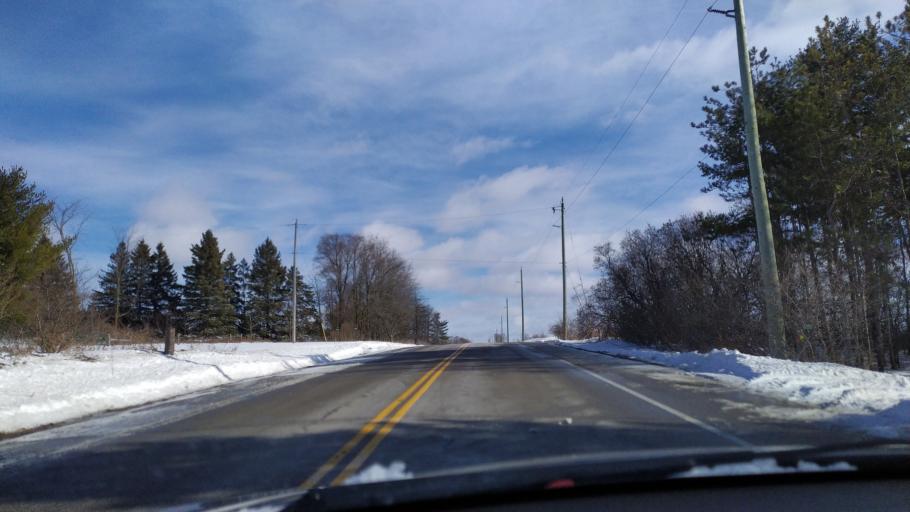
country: CA
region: Ontario
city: Waterloo
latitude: 43.4738
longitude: -80.7081
